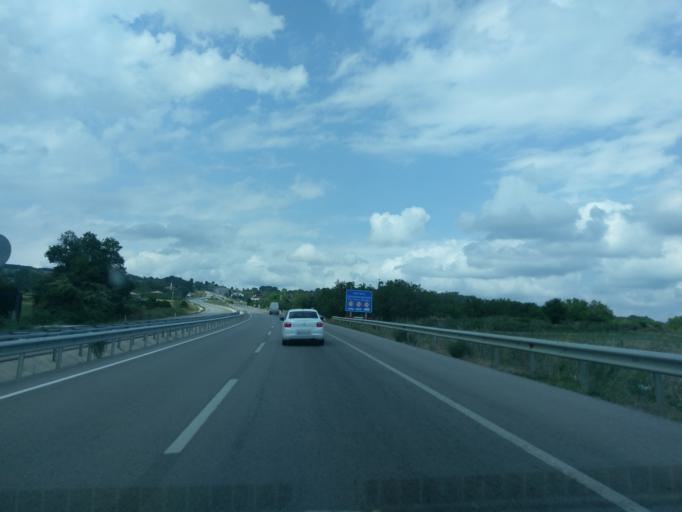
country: TR
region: Sinop
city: Kabali
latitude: 41.8455
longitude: 35.1372
